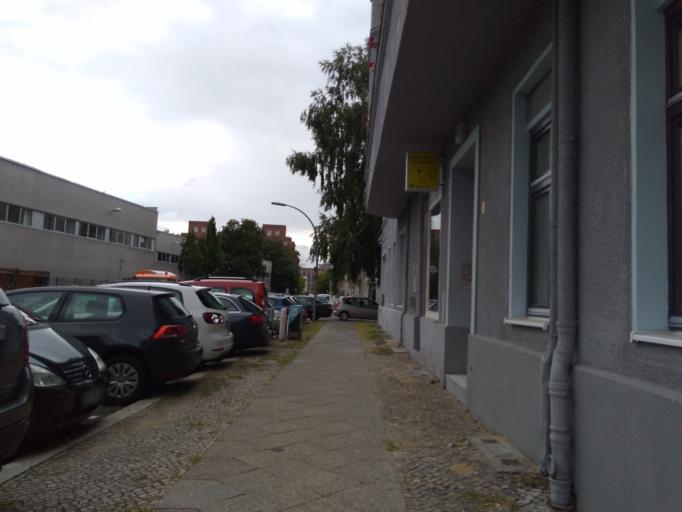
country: DE
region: Berlin
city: Siemensstadt
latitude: 52.5352
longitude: 13.2701
